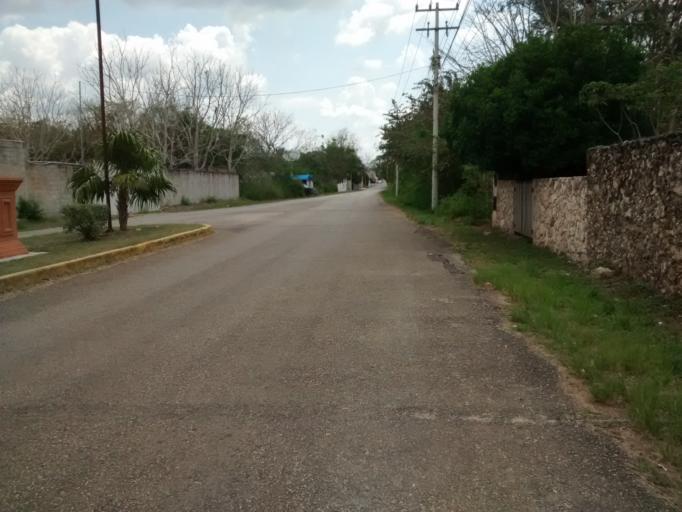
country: MX
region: Yucatan
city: Valladolid
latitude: 20.6866
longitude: -88.2196
